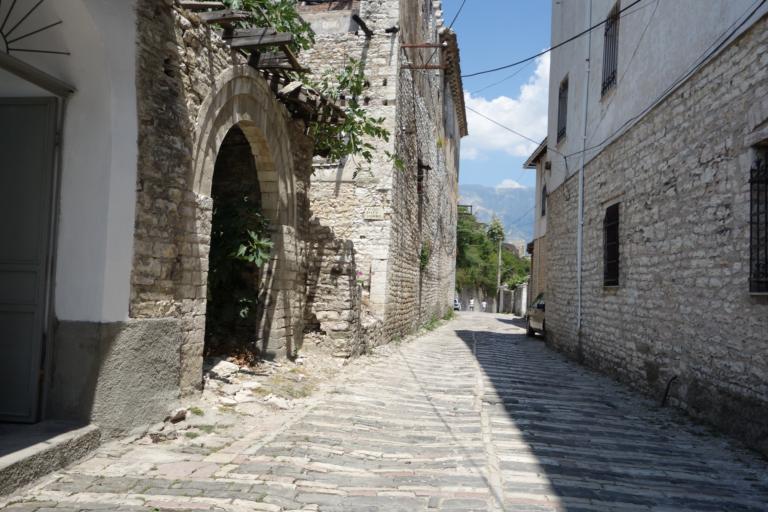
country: AL
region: Gjirokaster
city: Gjirokaster
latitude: 40.0773
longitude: 20.1405
